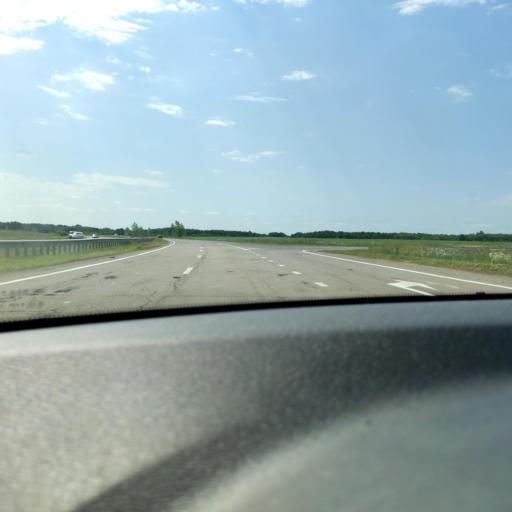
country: RU
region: Samara
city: Petra-Dubrava
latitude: 53.3388
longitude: 50.4348
